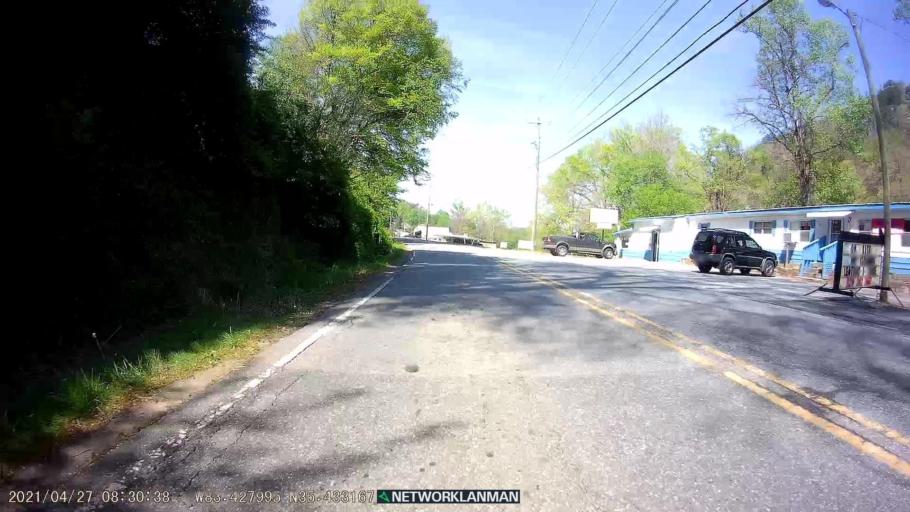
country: US
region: North Carolina
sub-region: Swain County
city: Bryson City
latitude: 35.4332
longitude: -83.4277
